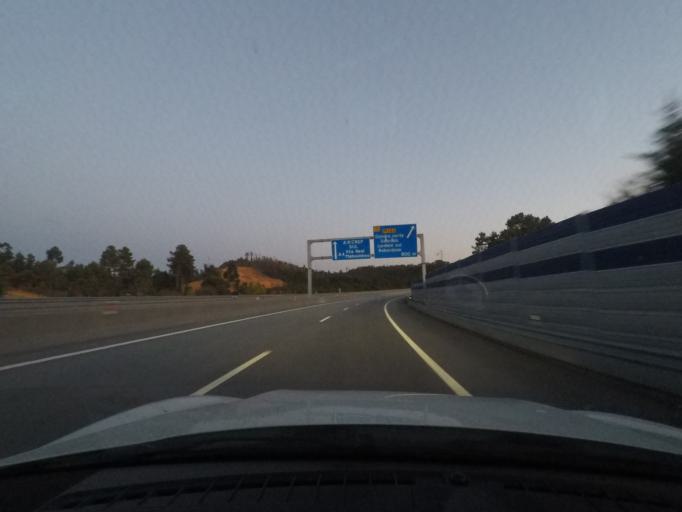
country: PT
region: Porto
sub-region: Valongo
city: Sobrado
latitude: 41.2231
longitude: -8.4503
